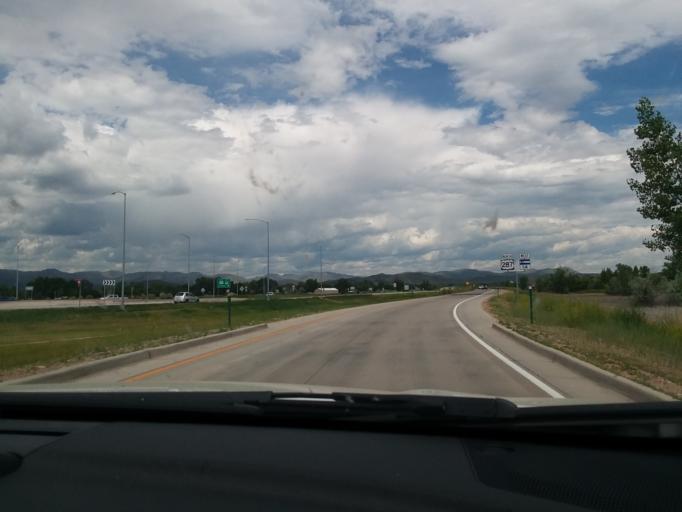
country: US
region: Colorado
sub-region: Larimer County
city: Laporte
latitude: 40.6261
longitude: -105.1054
